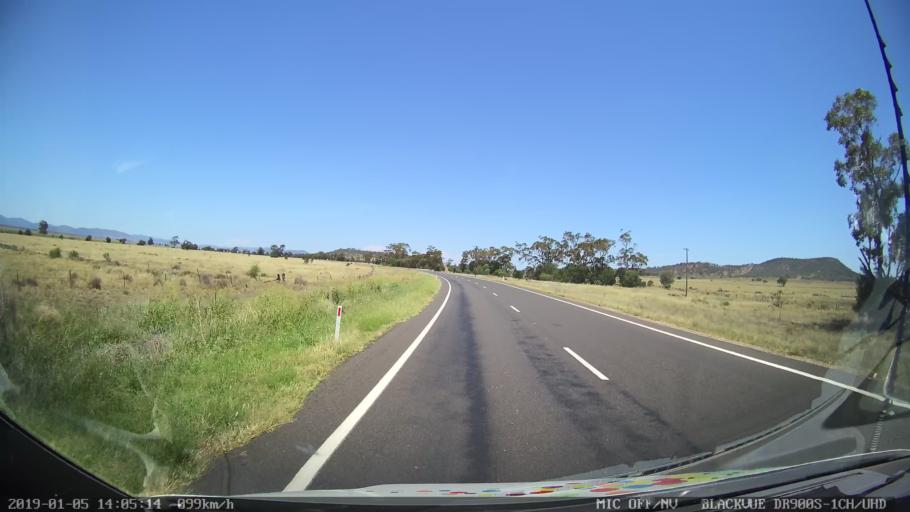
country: AU
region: New South Wales
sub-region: Gunnedah
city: Gunnedah
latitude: -31.2087
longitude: 150.3723
